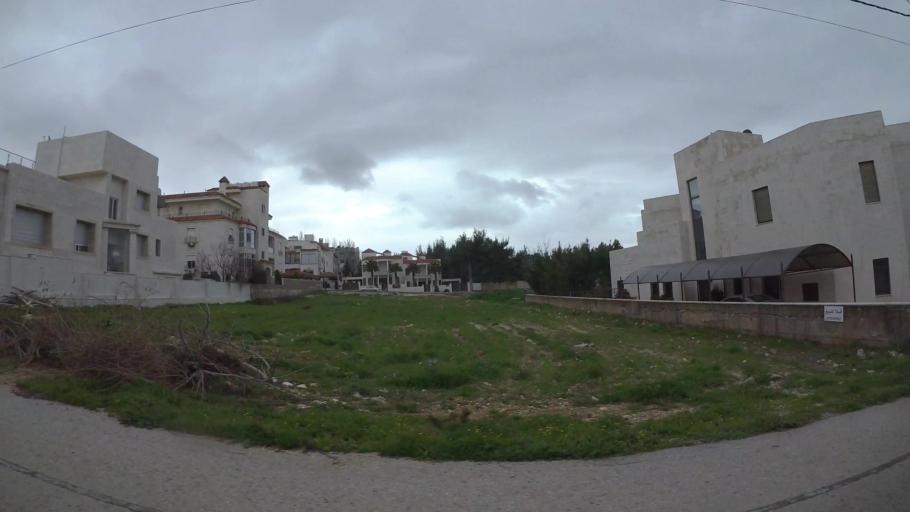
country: JO
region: Amman
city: Wadi as Sir
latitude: 31.9611
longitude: 35.8237
